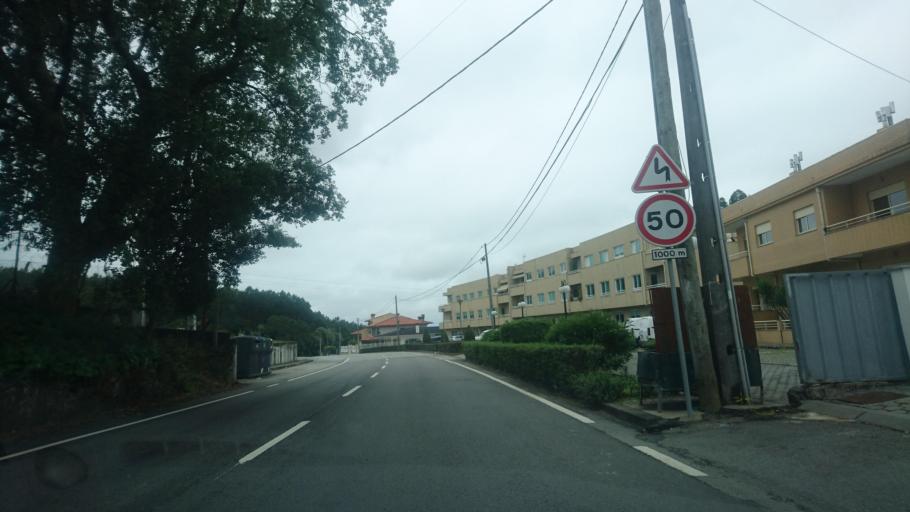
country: PT
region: Aveiro
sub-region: Santa Maria da Feira
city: Sao Joao de Ver
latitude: 40.9622
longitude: -8.5399
